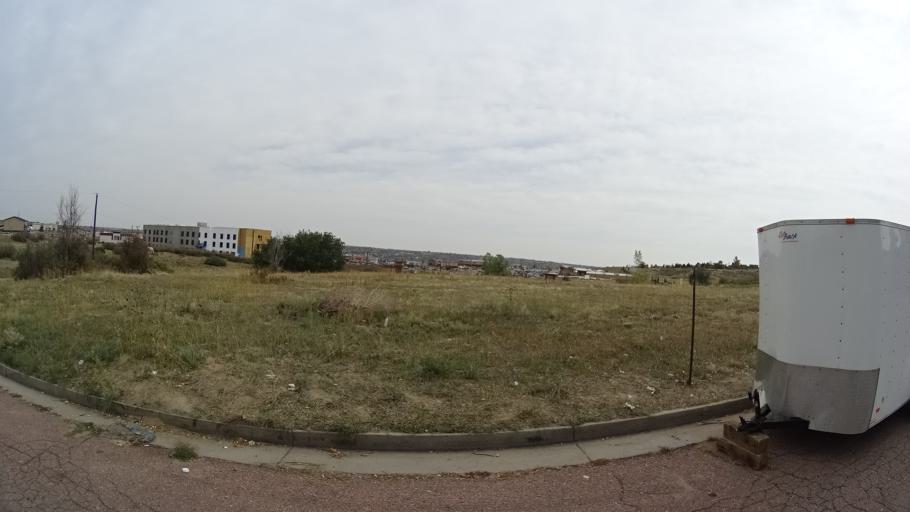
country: US
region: Colorado
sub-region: El Paso County
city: Cimarron Hills
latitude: 38.8959
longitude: -104.7247
